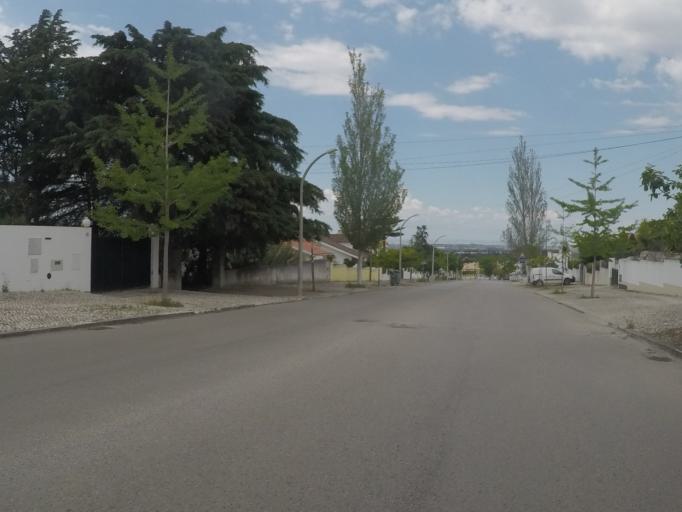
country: PT
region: Setubal
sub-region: Palmela
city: Quinta do Anjo
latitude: 38.5162
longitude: -9.0086
